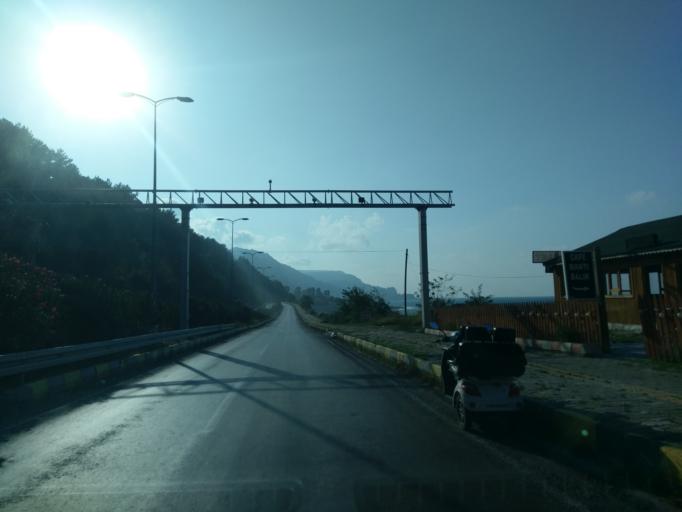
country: TR
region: Kastamonu
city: Catalzeytin
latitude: 41.9556
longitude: 34.2016
